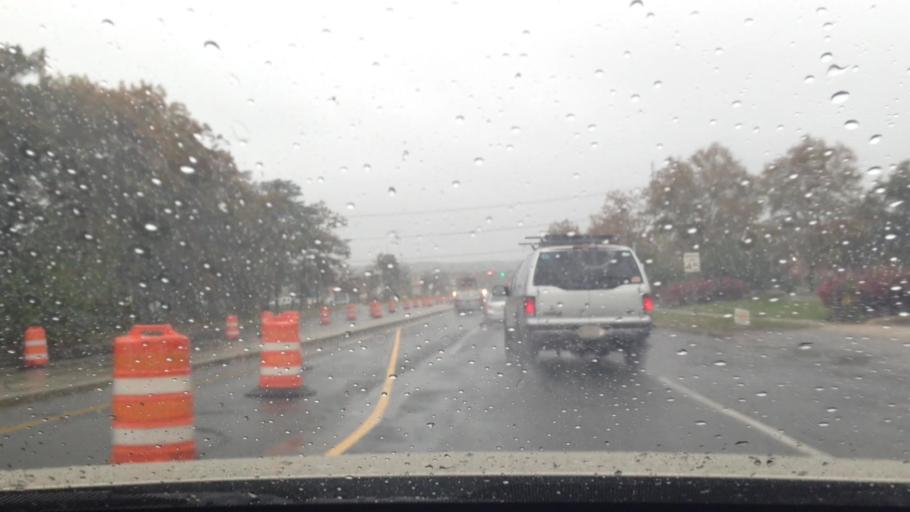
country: US
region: New York
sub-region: Suffolk County
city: Farmingville
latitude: 40.8245
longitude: -73.0203
